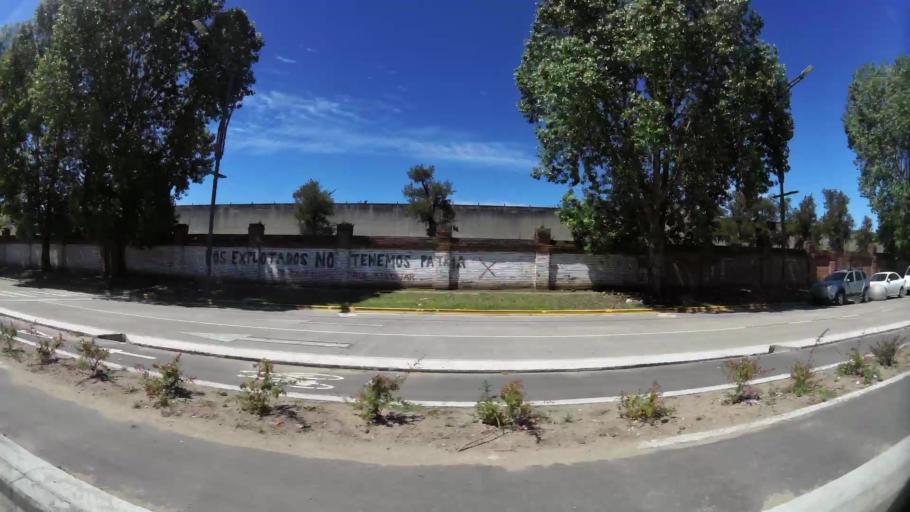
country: AR
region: Santa Fe
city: Perez
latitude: -32.9592
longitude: -60.7100
